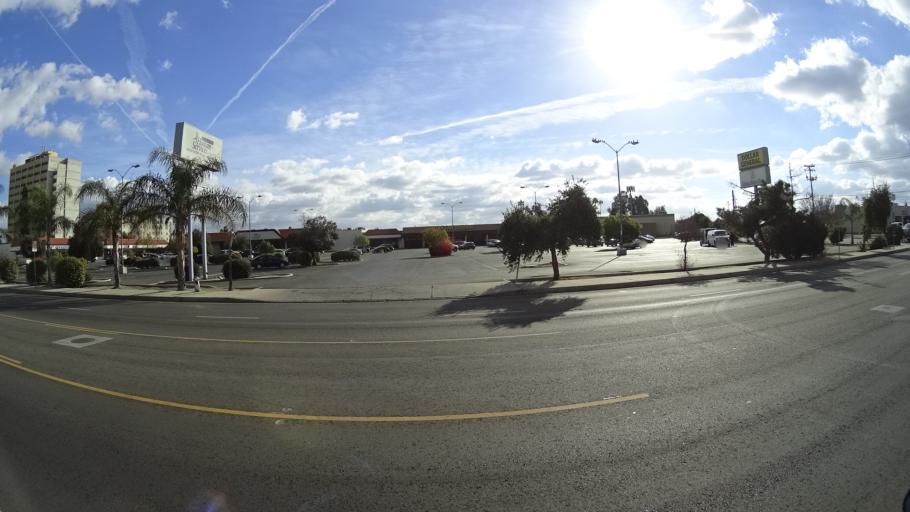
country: US
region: California
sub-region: Kern County
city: Bakersfield
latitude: 35.3322
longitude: -119.0376
